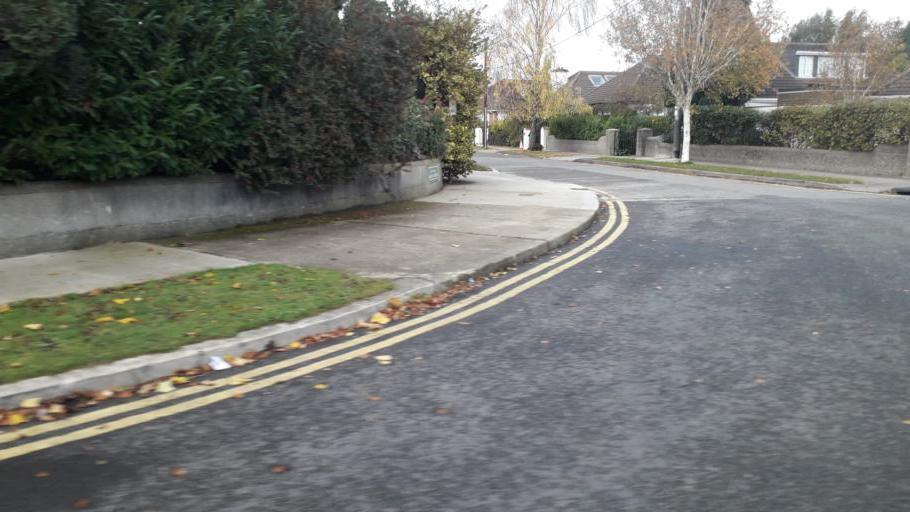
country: IE
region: Leinster
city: Mount Merrion
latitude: 53.3010
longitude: -6.2289
